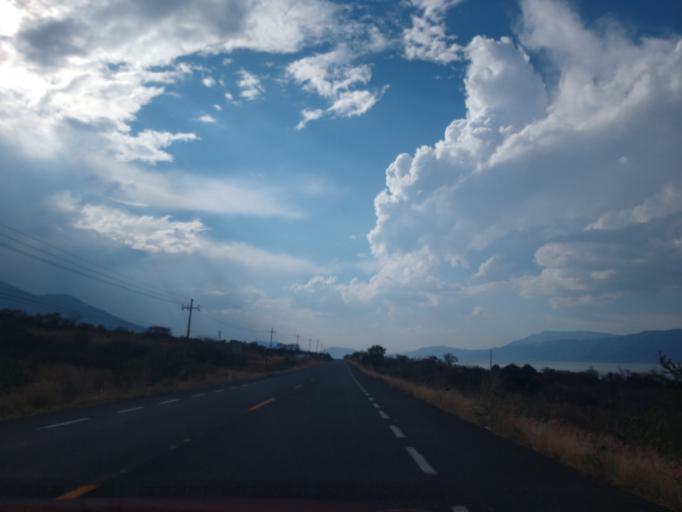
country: MX
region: Jalisco
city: Ajijic
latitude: 20.1919
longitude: -103.2607
